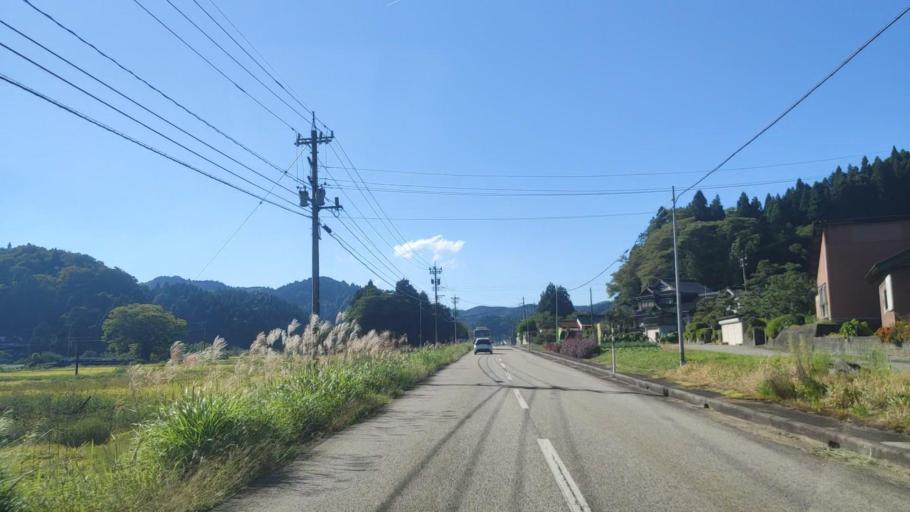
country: JP
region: Ishikawa
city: Nanao
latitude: 37.2787
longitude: 137.0503
